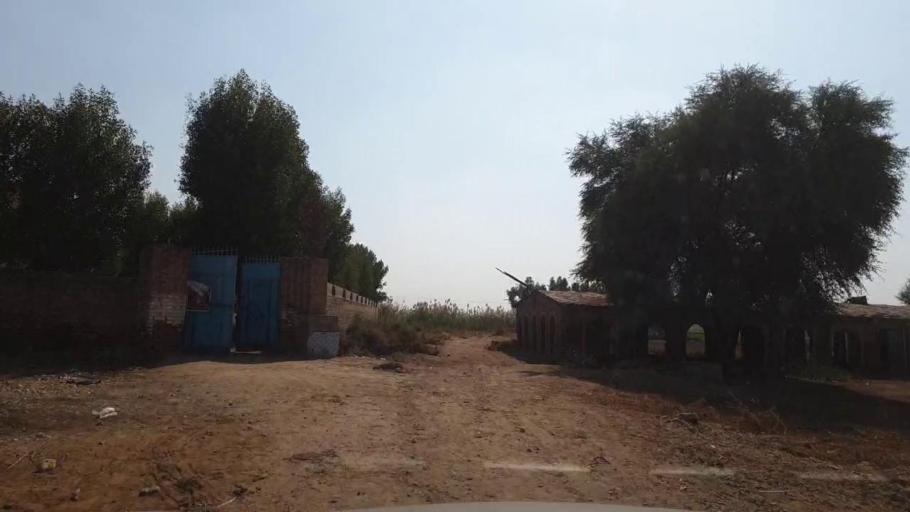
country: PK
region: Sindh
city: Tando Allahyar
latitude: 25.5521
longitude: 68.7111
